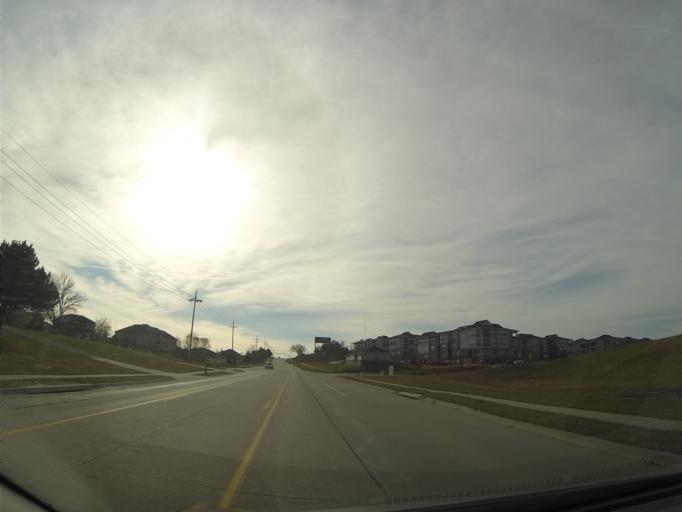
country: US
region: Nebraska
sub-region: Douglas County
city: Elkhorn
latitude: 41.2707
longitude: -96.2157
